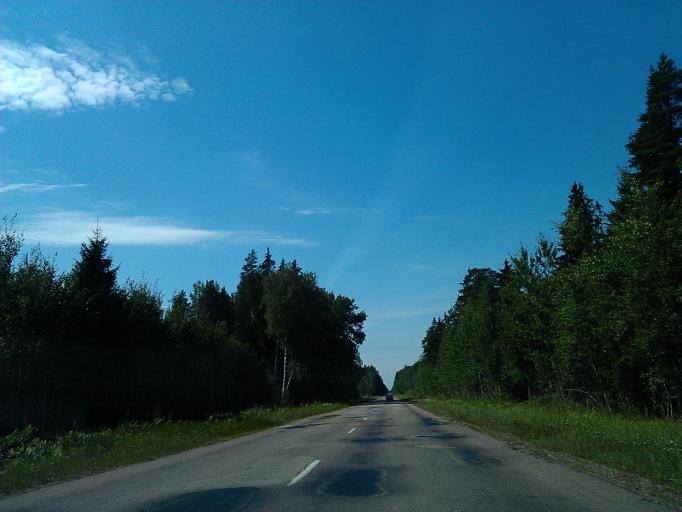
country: LV
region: Ropazu
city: Ropazi
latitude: 56.9512
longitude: 24.5203
